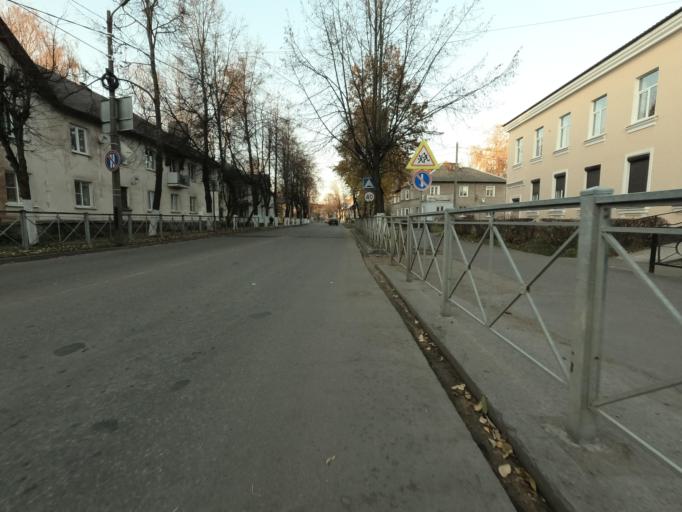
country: RU
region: Leningrad
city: Kirovsk
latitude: 59.8734
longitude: 30.9904
